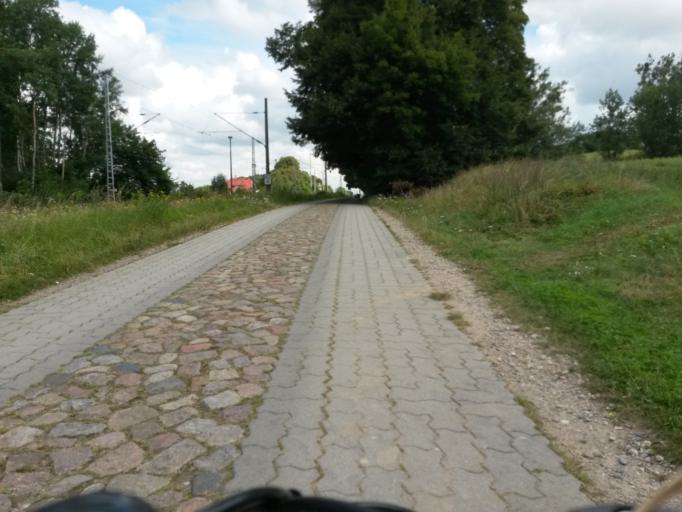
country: DE
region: Brandenburg
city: Pinnow
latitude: 53.1028
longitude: 14.0305
